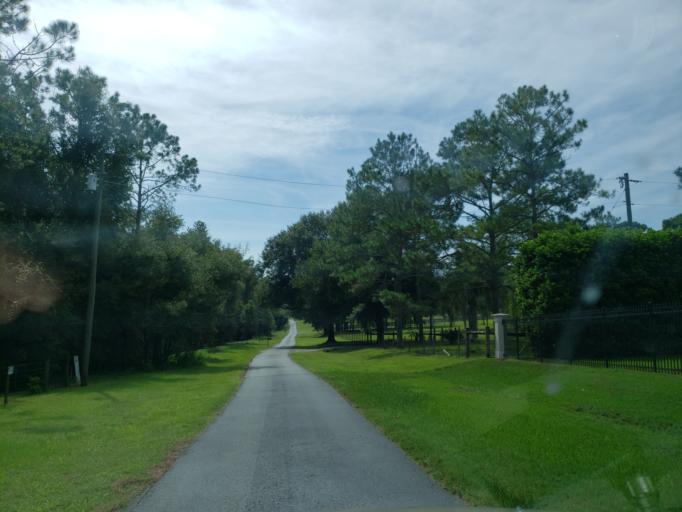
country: US
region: Florida
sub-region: Hernando County
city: Hill 'n Dale
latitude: 28.4587
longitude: -82.2634
